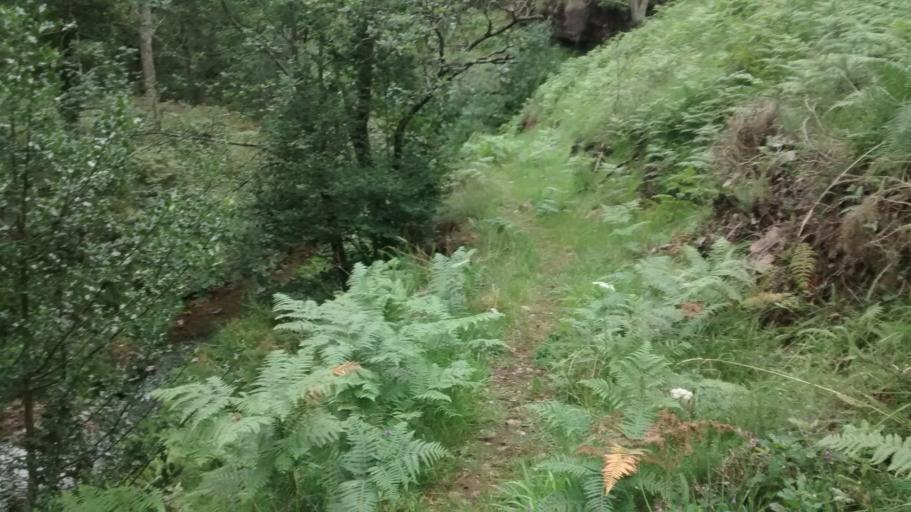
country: ES
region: Cantabria
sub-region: Provincia de Cantabria
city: Ruente
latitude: 43.1972
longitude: -4.2213
